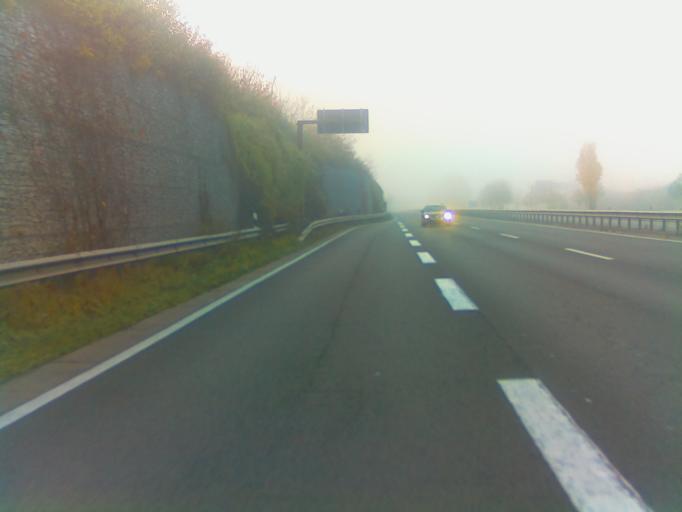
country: DE
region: Rheinland-Pfalz
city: Frankenthal
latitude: 49.4903
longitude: 8.3573
